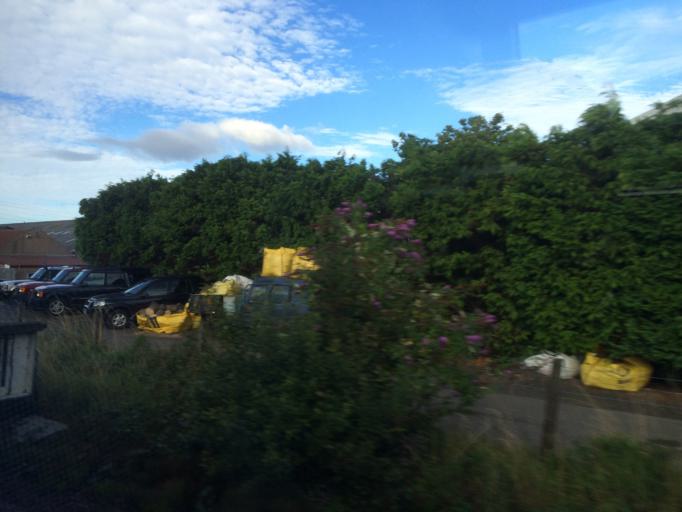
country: GB
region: Scotland
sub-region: Falkirk
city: Larbert
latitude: 56.0134
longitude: -3.8333
